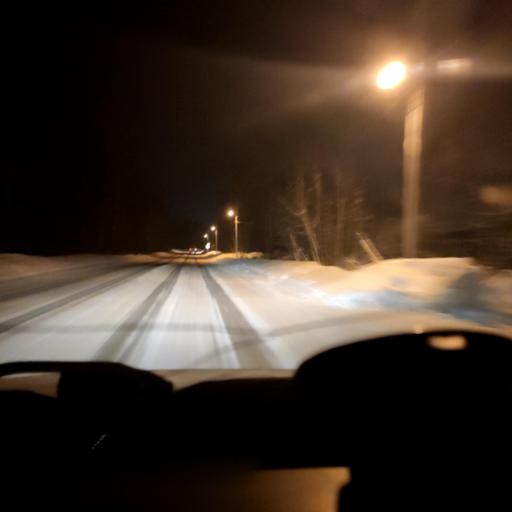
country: RU
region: Perm
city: Krasnokamsk
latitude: 58.0987
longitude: 55.7557
